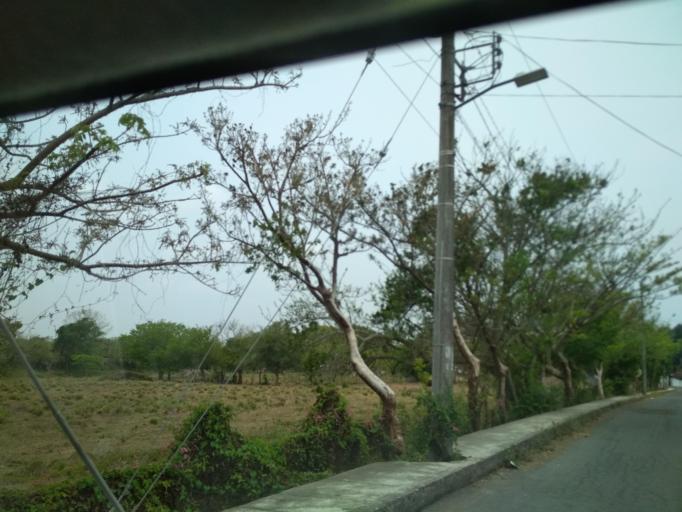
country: MX
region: Veracruz
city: Paso del Toro
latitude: 19.0499
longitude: -96.1521
